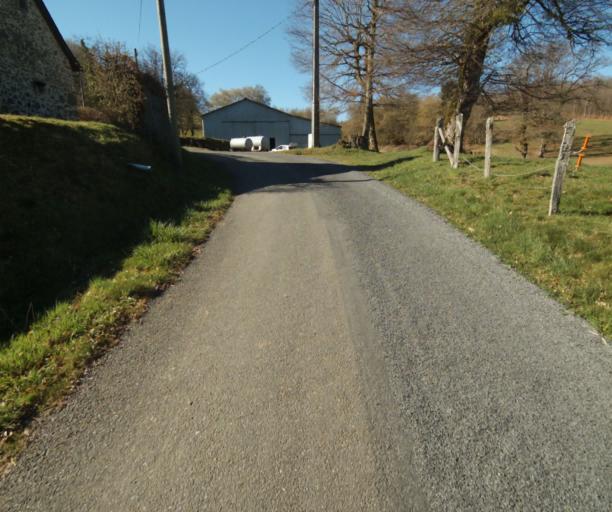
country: FR
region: Limousin
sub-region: Departement de la Correze
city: Seilhac
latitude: 45.3974
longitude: 1.6996
